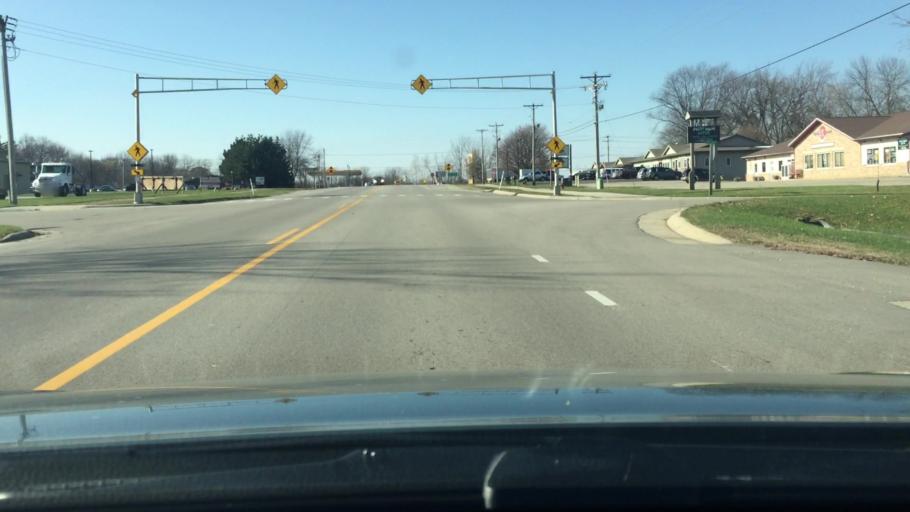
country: US
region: Wisconsin
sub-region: Jefferson County
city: Cambridge
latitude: 43.0088
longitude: -89.0196
